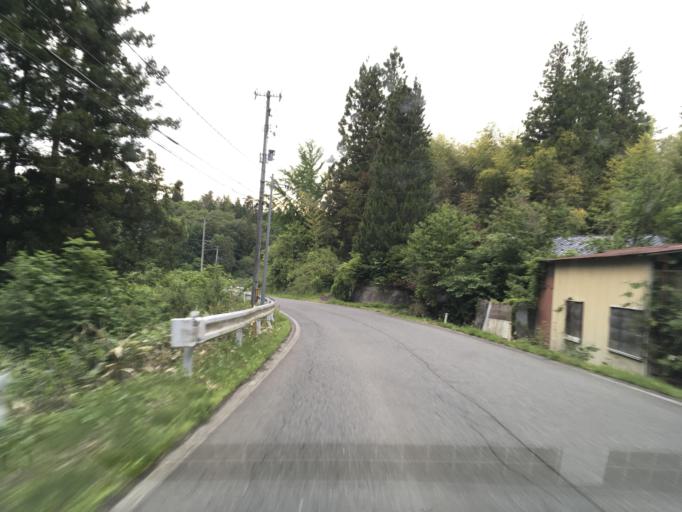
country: JP
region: Iwate
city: Mizusawa
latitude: 39.1662
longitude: 141.3042
